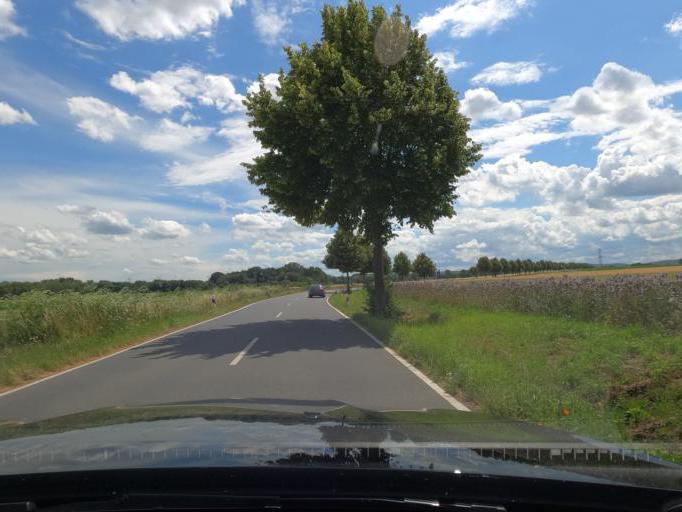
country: DE
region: Lower Saxony
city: Lengede
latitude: 52.1853
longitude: 10.3173
